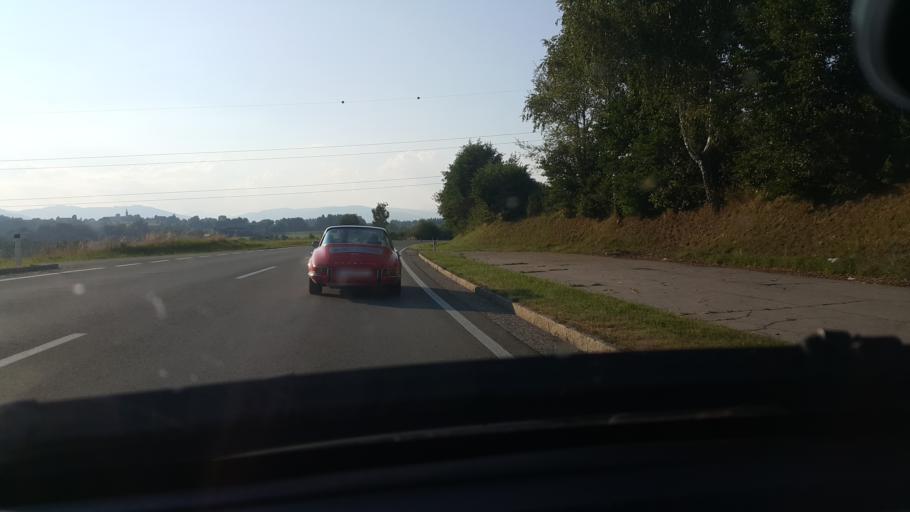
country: AT
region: Carinthia
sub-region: Politischer Bezirk Klagenfurt Land
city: Moosburg
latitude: 46.6744
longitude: 14.1571
